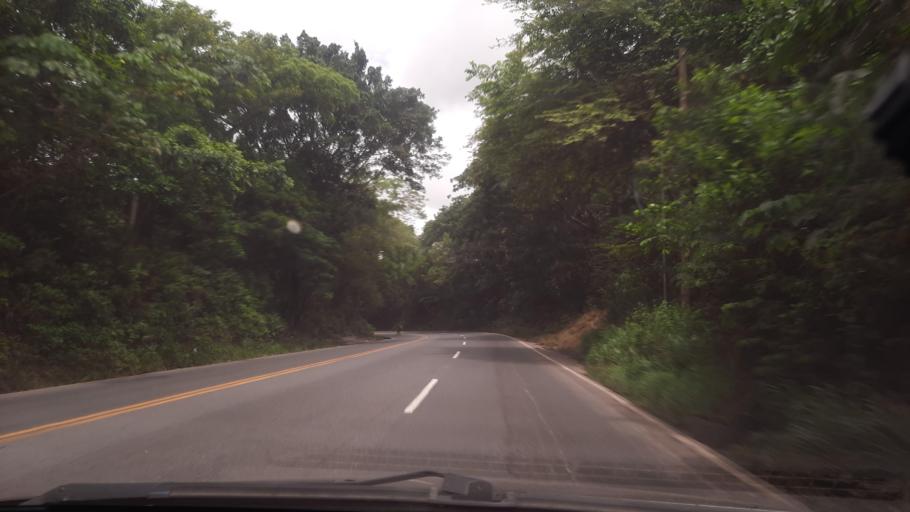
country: GT
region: Izabal
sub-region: Municipio de Los Amates
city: Los Amates
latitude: 15.2326
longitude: -89.2076
